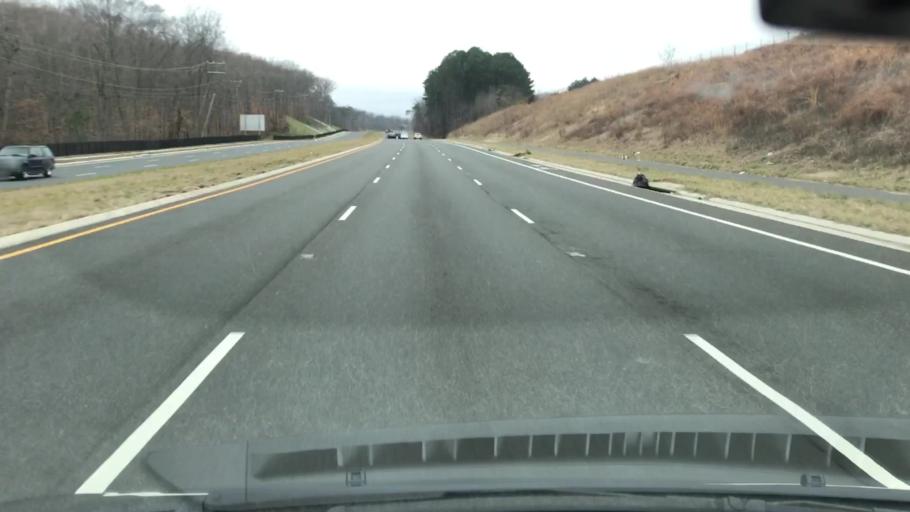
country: US
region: Virginia
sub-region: Fairfax County
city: Fort Belvoir
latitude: 38.7079
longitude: -77.1711
